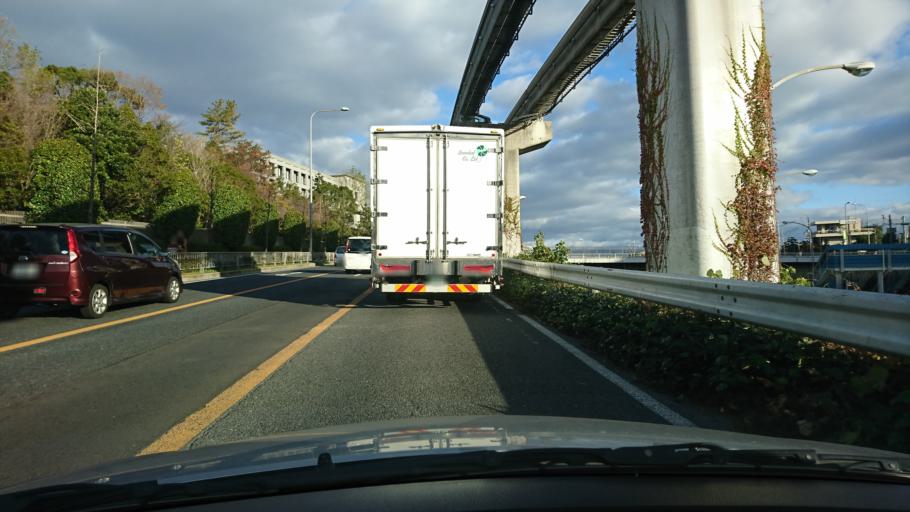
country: JP
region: Osaka
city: Toyonaka
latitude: 34.8014
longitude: 135.4536
